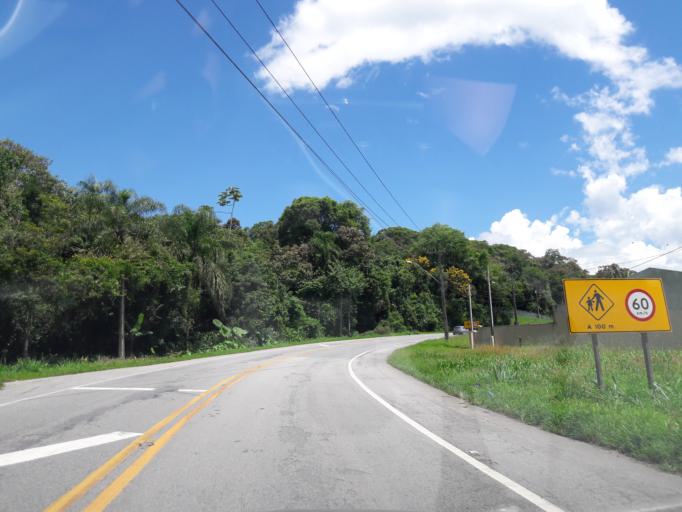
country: BR
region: Parana
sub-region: Antonina
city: Antonina
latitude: -25.4609
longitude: -48.8184
